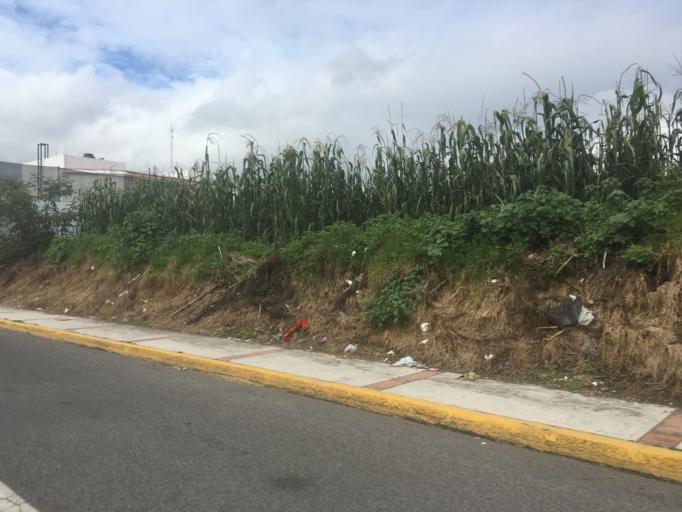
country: MX
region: Morelos
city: Metepec
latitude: 19.2648
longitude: -99.6076
